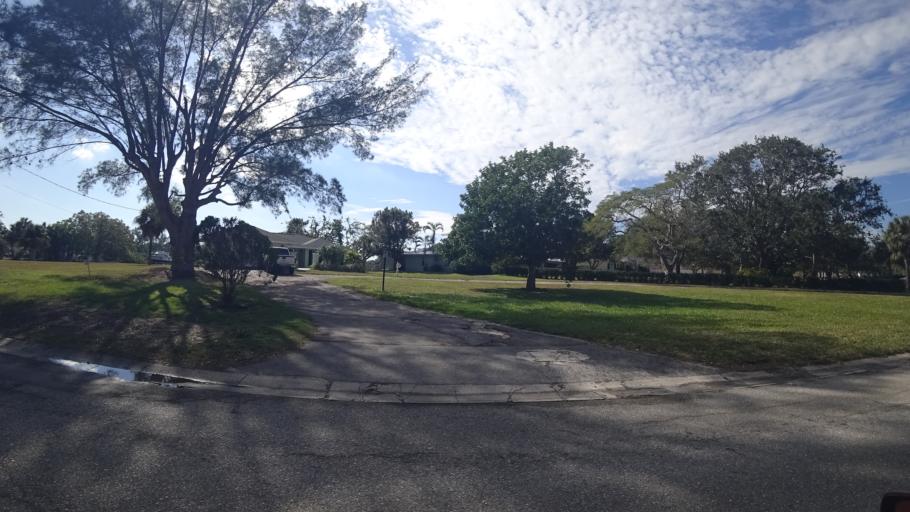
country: US
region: Florida
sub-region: Manatee County
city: West Bradenton
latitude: 27.5122
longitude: -82.6202
